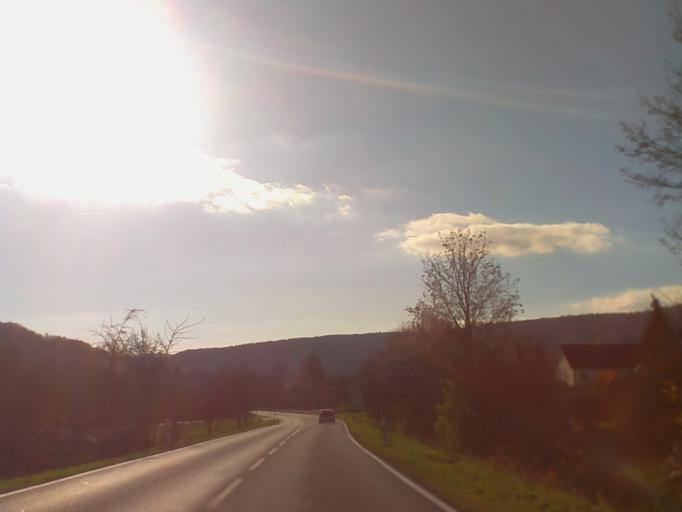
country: DE
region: Bavaria
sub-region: Regierungsbezirk Unterfranken
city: Bad Bocklet
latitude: 50.2599
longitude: 10.0684
